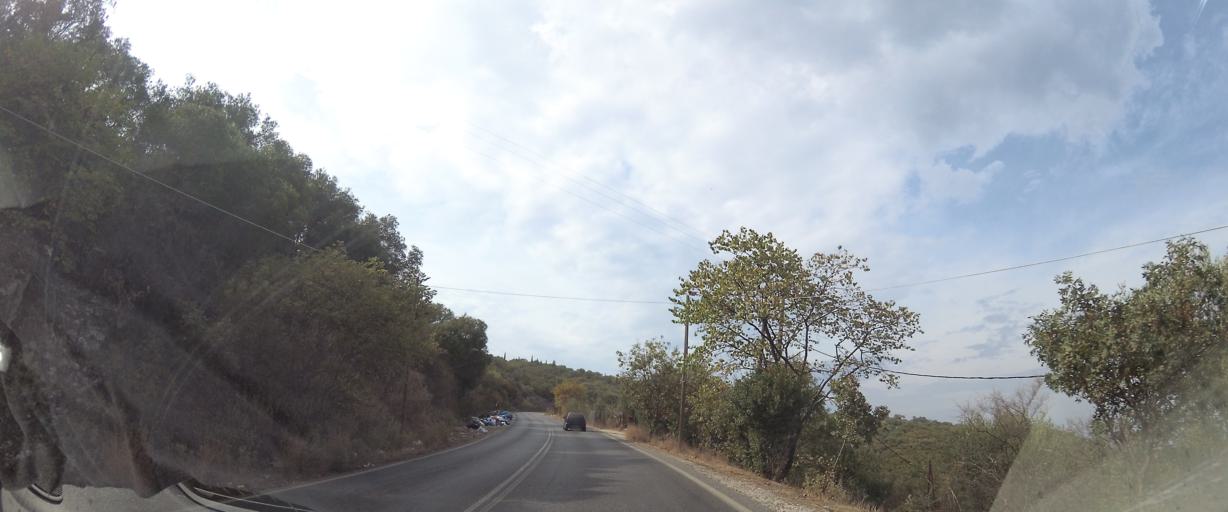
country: GR
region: Ionian Islands
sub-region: Nomos Kerkyras
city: Acharavi
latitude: 39.8016
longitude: 19.8795
